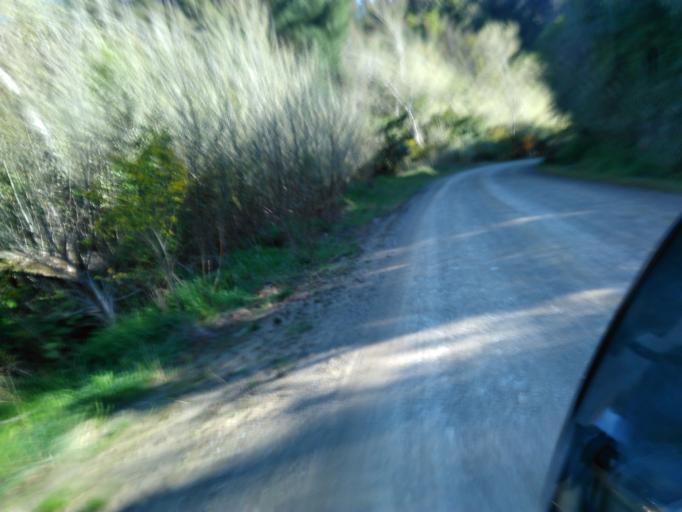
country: NZ
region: Gisborne
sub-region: Gisborne District
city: Gisborne
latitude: -38.4124
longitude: 177.6910
